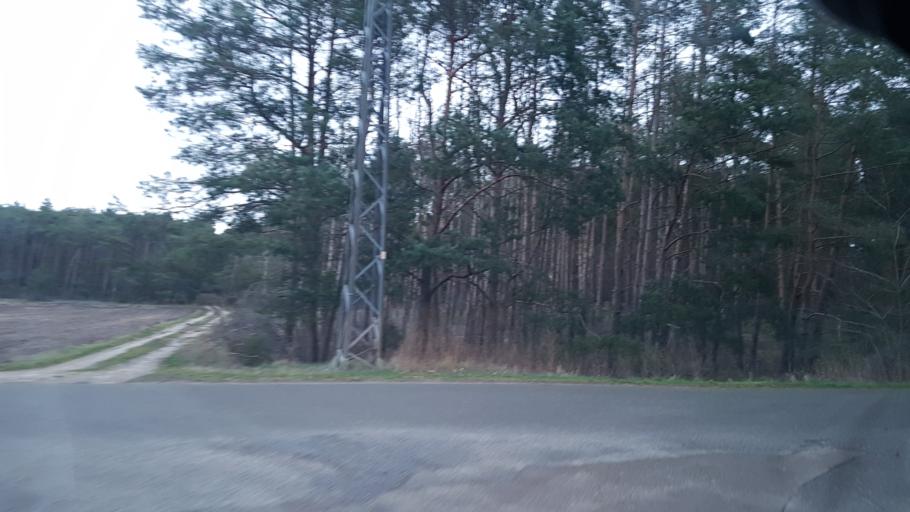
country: DE
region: Brandenburg
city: Schlieben
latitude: 51.7148
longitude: 13.3134
